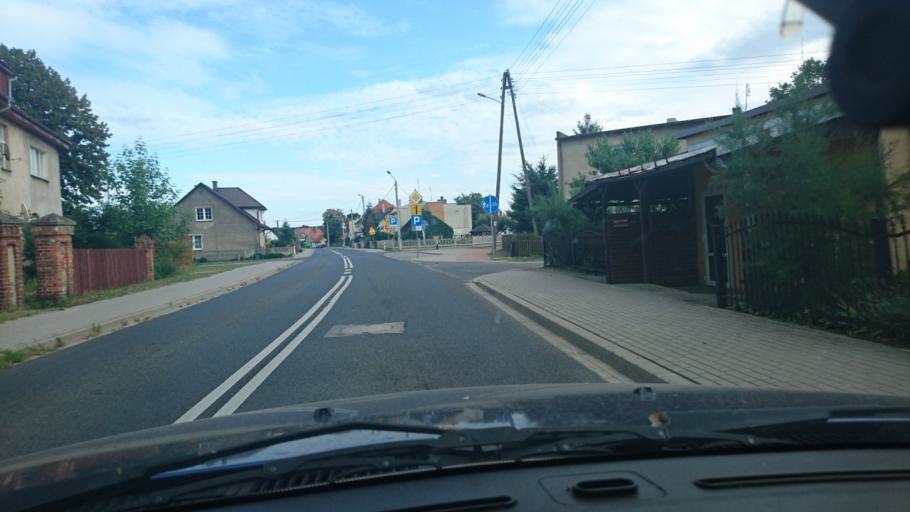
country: PL
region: Greater Poland Voivodeship
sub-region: Powiat ostrowski
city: Jankow Przygodzki
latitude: 51.5044
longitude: 17.7701
